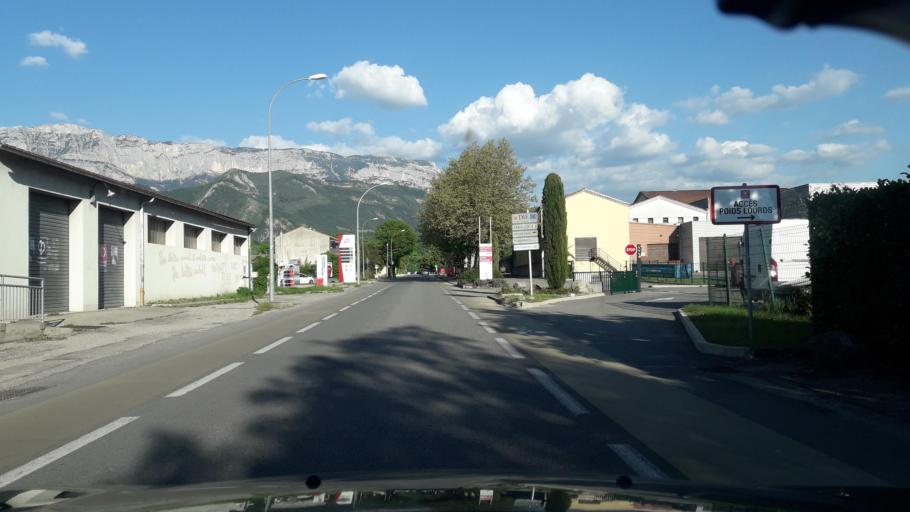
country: FR
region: Rhone-Alpes
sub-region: Departement de la Drome
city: Die
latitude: 44.7610
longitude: 5.3556
